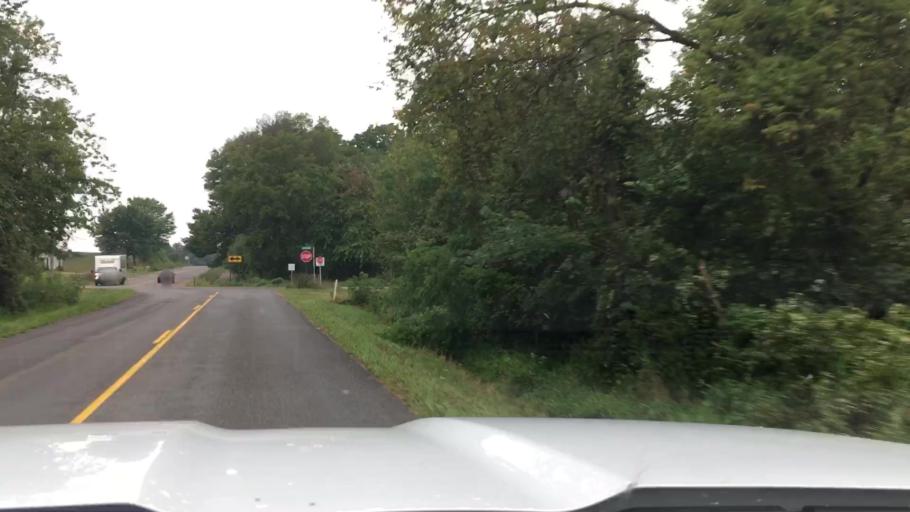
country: US
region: Michigan
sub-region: Kent County
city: Byron Center
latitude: 42.8410
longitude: -85.7815
